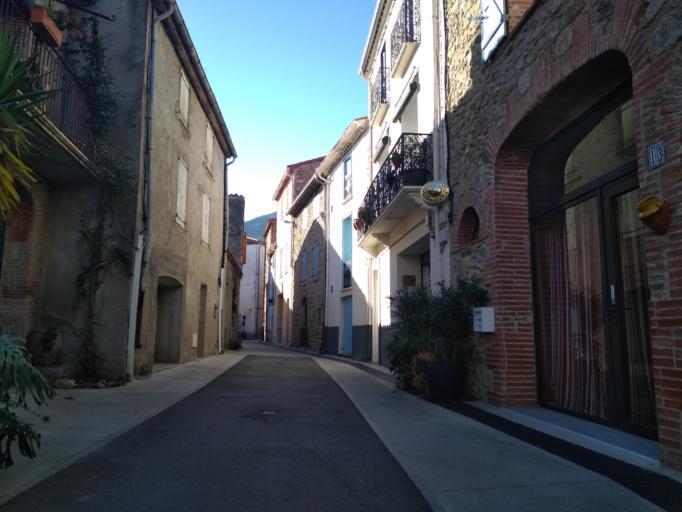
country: FR
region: Languedoc-Roussillon
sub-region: Departement des Pyrenees-Orientales
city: la Roca d'Albera
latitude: 42.5229
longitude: 2.9338
